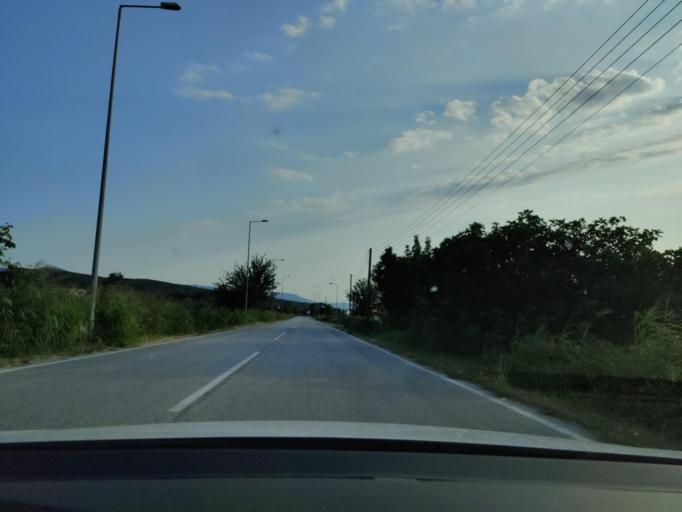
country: GR
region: East Macedonia and Thrace
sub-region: Nomos Kavalas
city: Amygdaleonas
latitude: 40.9803
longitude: 24.3669
